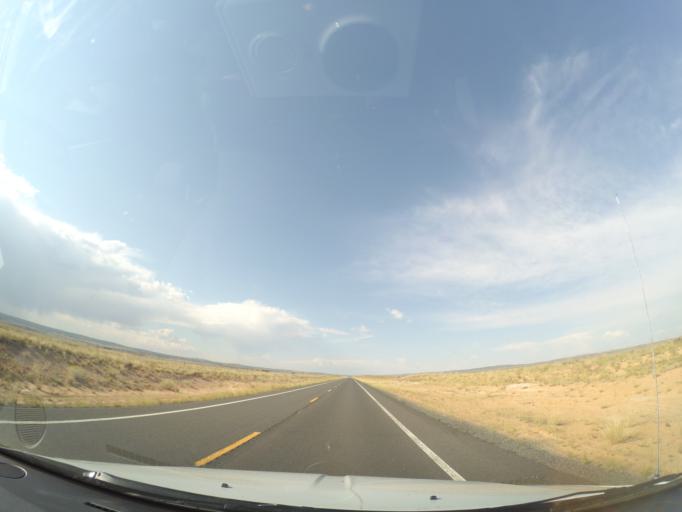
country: US
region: Arizona
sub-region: Coconino County
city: Tuba City
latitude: 36.4183
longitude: -111.4237
